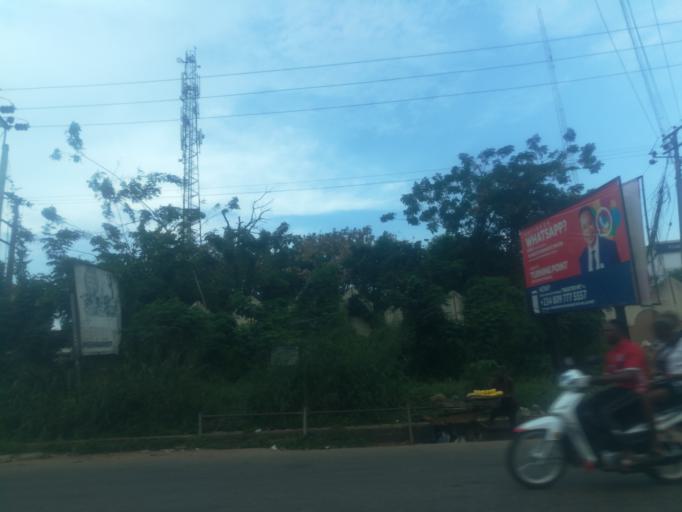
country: NG
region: Oyo
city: Ibadan
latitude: 7.4278
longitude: 3.8940
